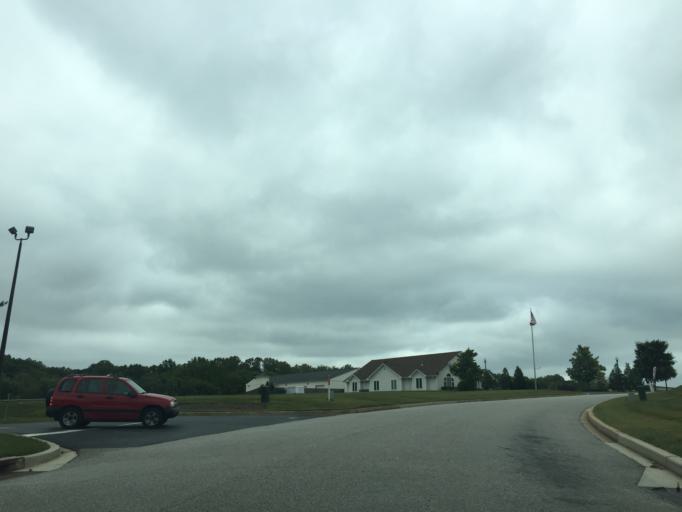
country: US
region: Maryland
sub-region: Harford County
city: Bel Air North
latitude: 39.5692
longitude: -76.3624
